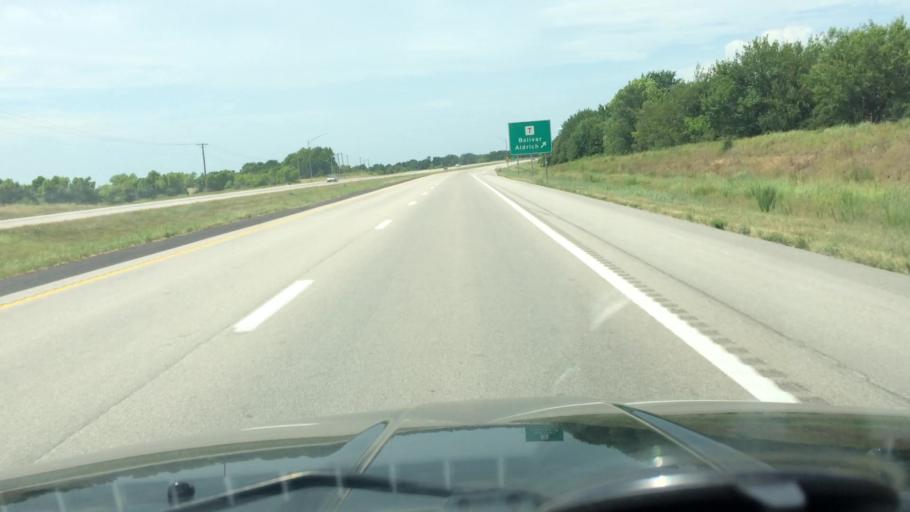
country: US
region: Missouri
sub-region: Polk County
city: Bolivar
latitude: 37.5890
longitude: -93.4255
